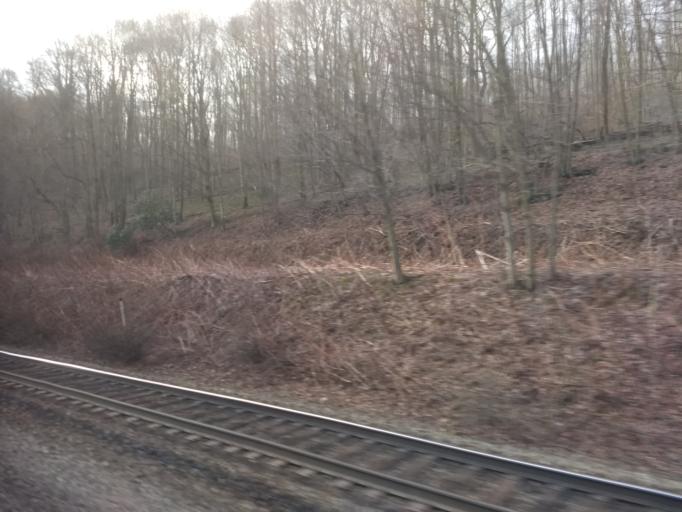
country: US
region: Pennsylvania
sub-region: Cambria County
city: Vinco
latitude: 40.3730
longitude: -78.8289
